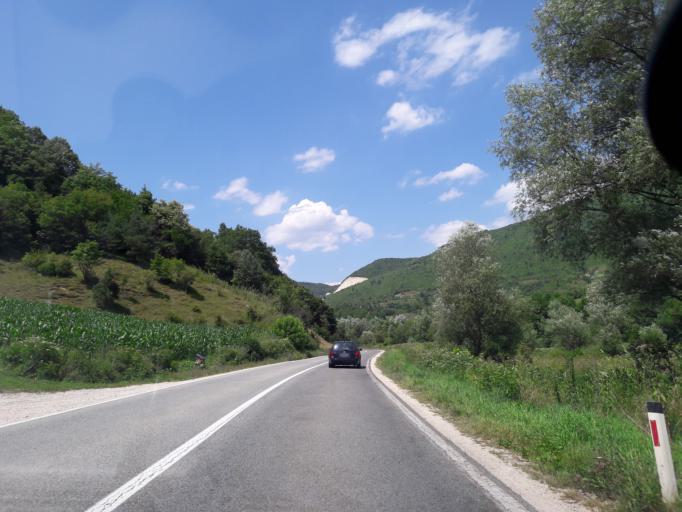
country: BA
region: Republika Srpska
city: Mrkonjic Grad
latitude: 44.3580
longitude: 17.1619
